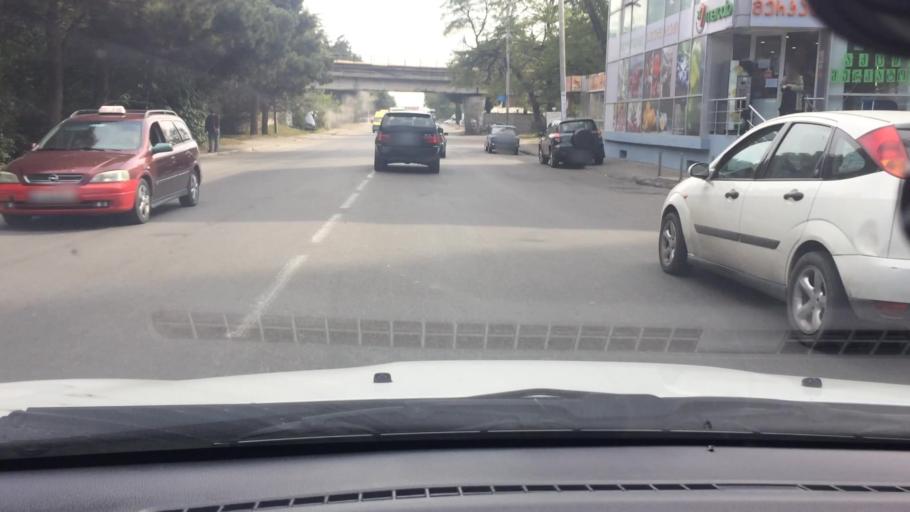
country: GE
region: T'bilisi
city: Tbilisi
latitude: 41.6447
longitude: 44.9116
